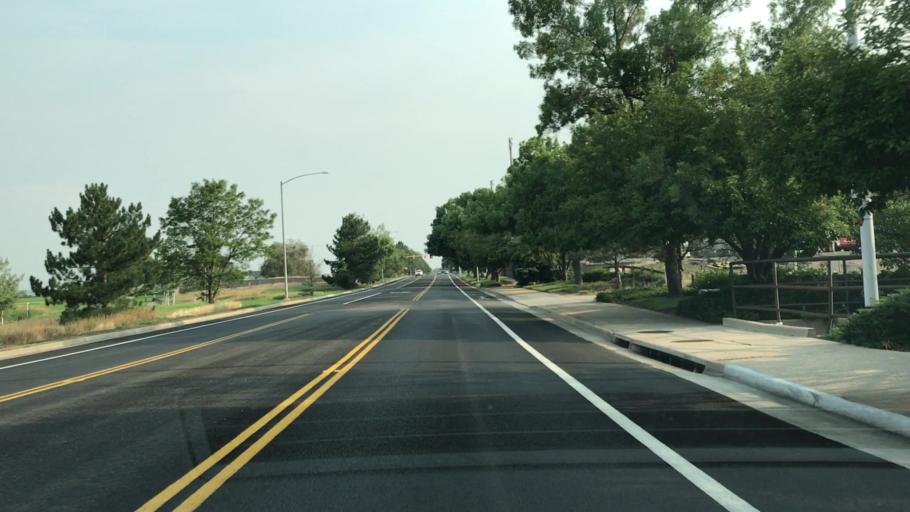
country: US
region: Colorado
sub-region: Broomfield County
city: Broomfield
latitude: 39.9314
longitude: -105.0719
